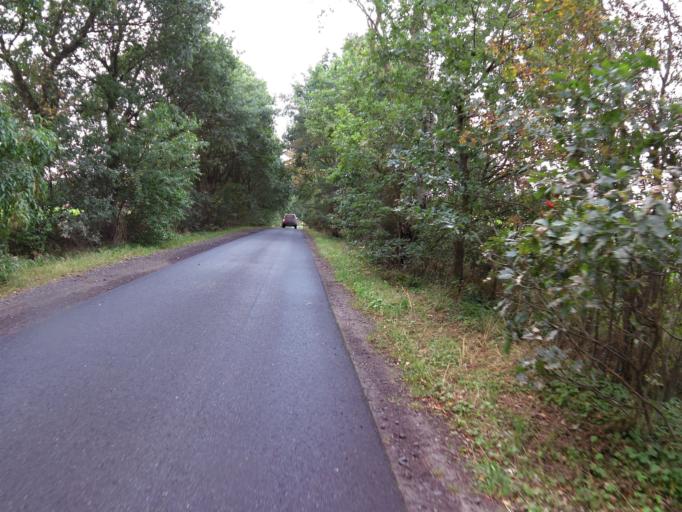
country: DE
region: Lower Saxony
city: Helvesiek
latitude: 53.1998
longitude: 9.4627
